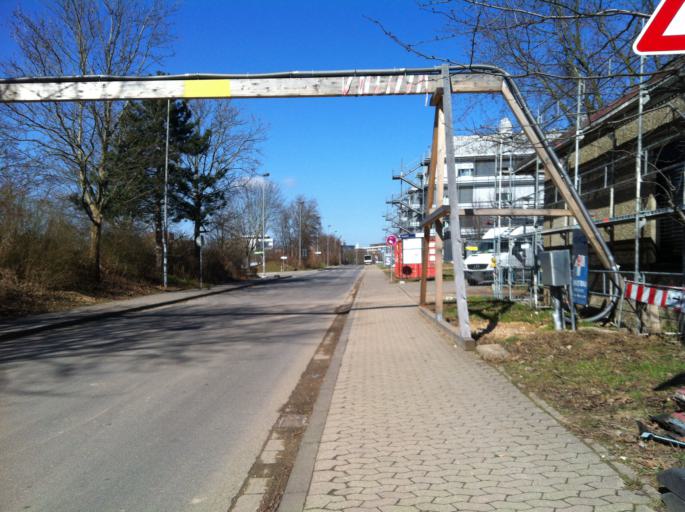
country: DE
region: Rheinland-Pfalz
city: Mainz
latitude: 49.9902
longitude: 8.2317
